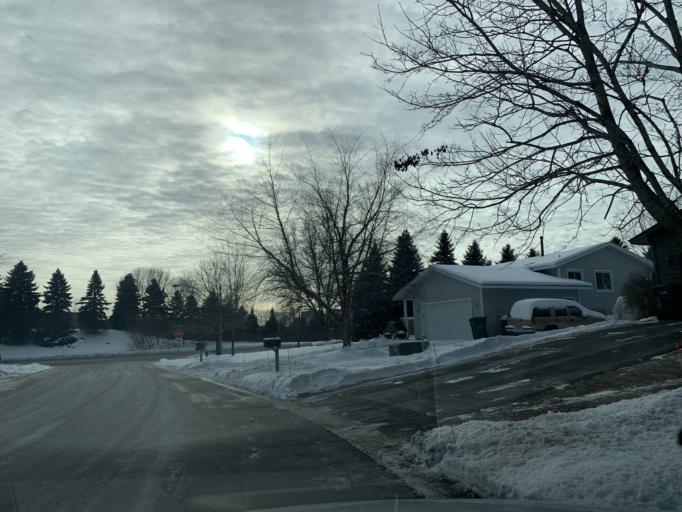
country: US
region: Minnesota
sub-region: Dakota County
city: Burnsville
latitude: 44.7529
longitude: -93.2903
